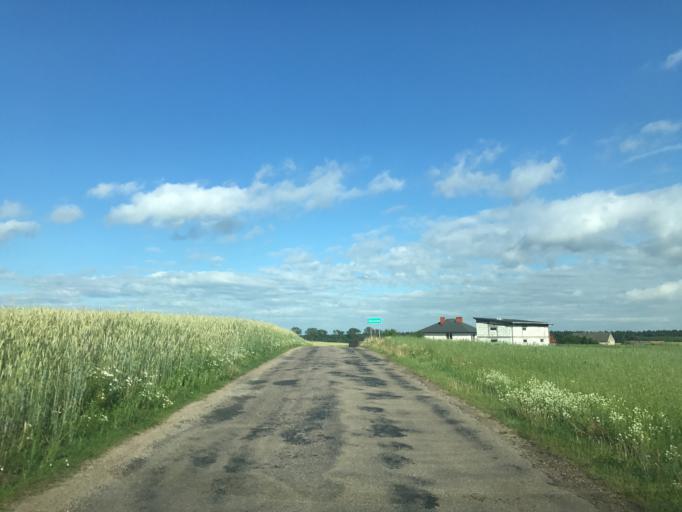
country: PL
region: Warmian-Masurian Voivodeship
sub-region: Powiat dzialdowski
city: Rybno
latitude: 53.3767
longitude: 19.8587
